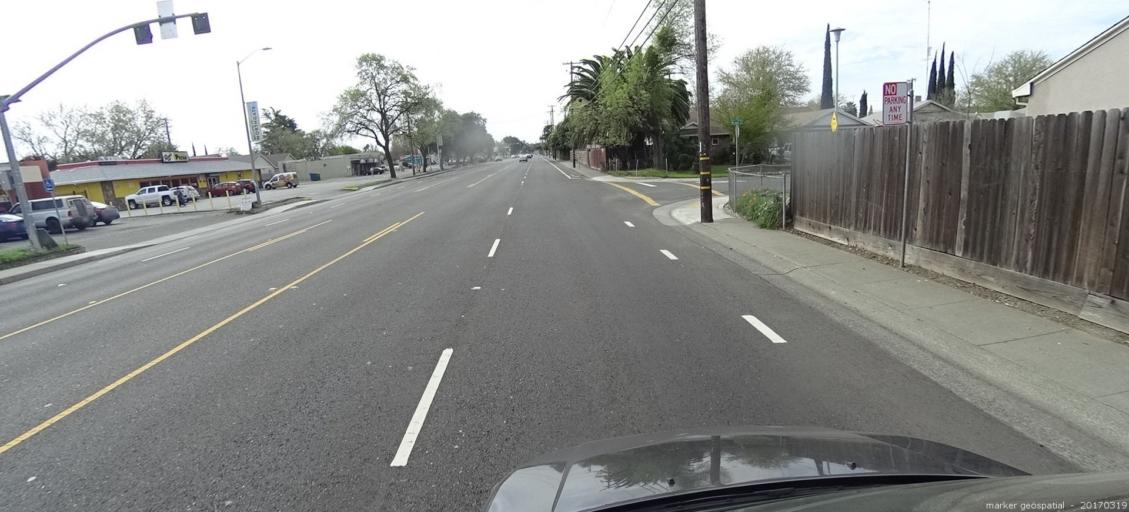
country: US
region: California
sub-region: Sacramento County
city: Sacramento
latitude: 38.6138
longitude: -121.4756
